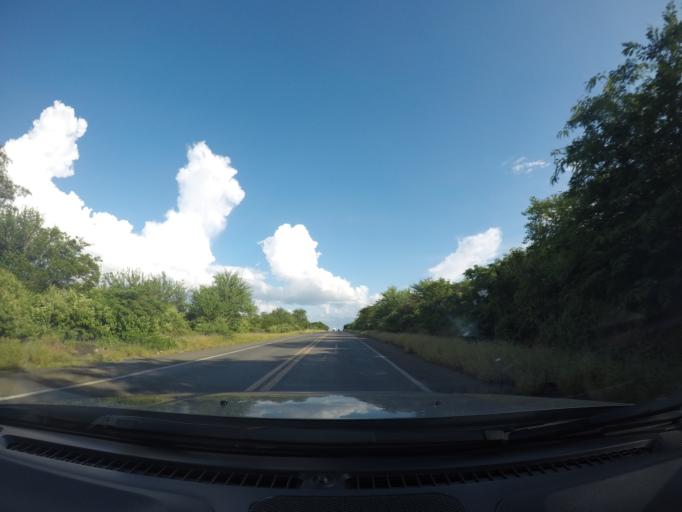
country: BR
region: Bahia
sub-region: Oliveira Dos Brejinhos
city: Oliveira dos Brejinhos
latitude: -12.0690
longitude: -42.9557
